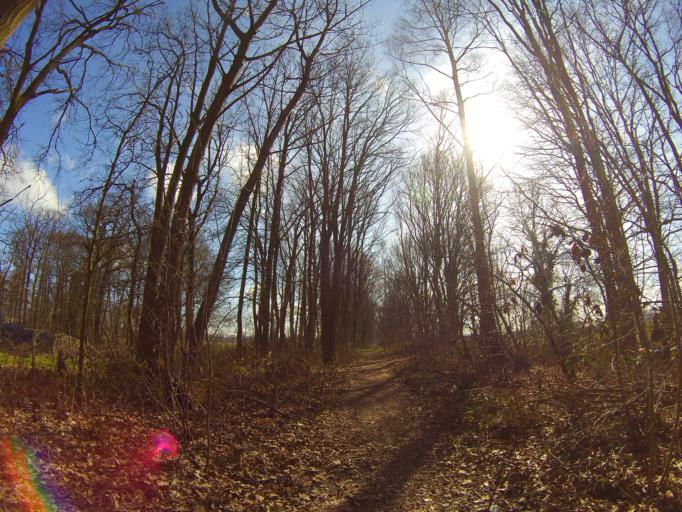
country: NL
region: Utrecht
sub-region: Gemeente Utrechtse Heuvelrug
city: Overberg
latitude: 52.0681
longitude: 5.4614
